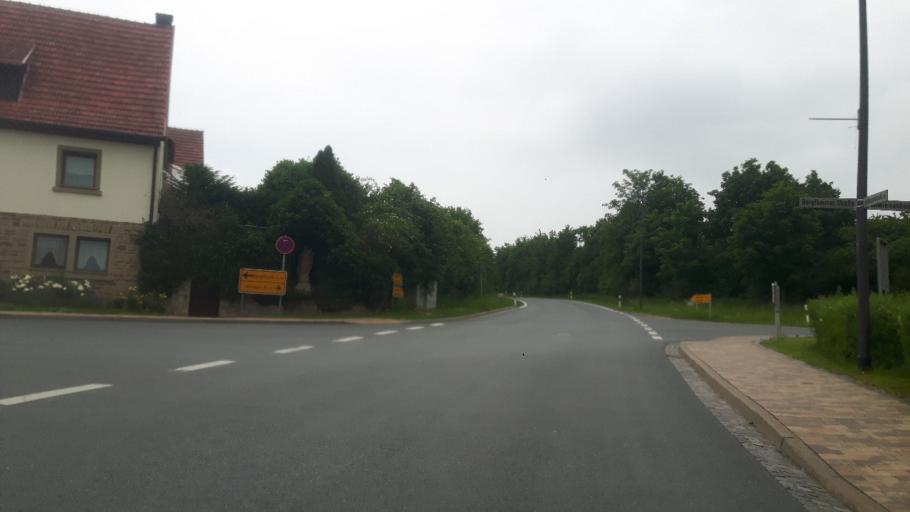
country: DE
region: Bavaria
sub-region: Regierungsbezirk Unterfranken
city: Schwanfeld
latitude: 49.8990
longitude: 10.1251
